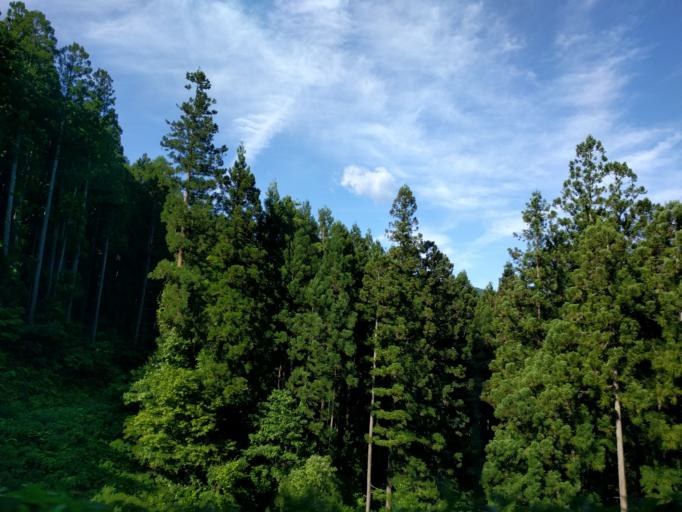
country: JP
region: Fukushima
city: Kitakata
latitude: 37.3859
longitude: 139.8291
